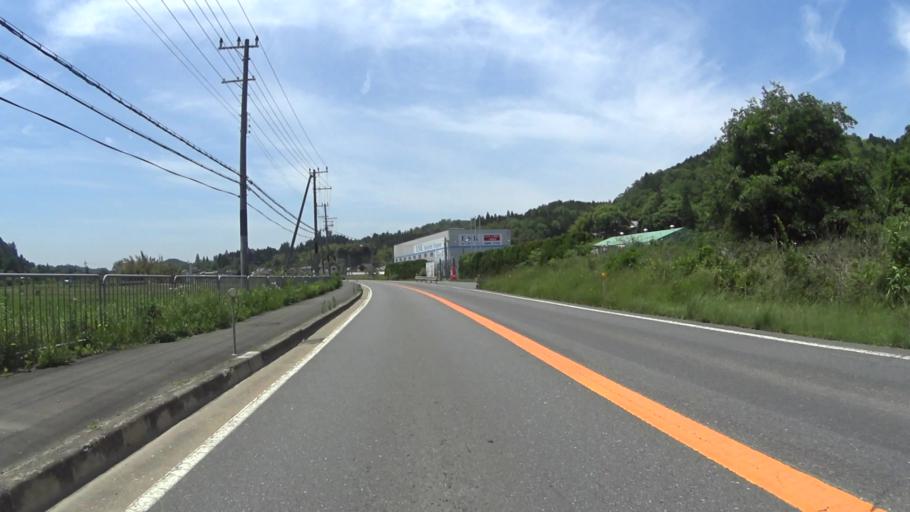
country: JP
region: Kyoto
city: Ayabe
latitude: 35.1799
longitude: 135.3892
